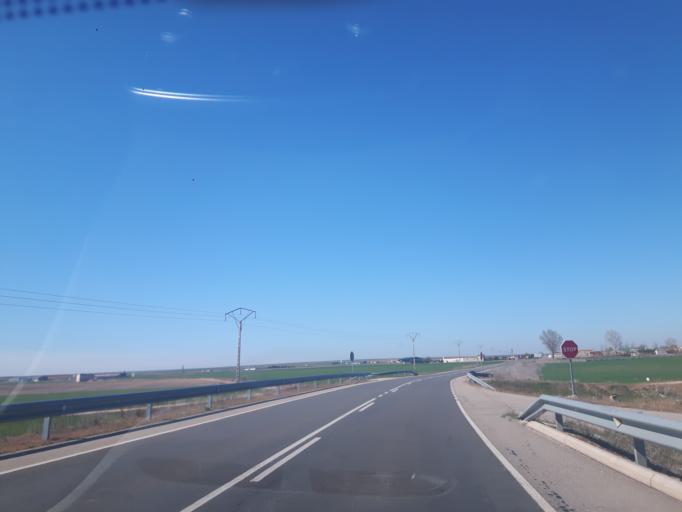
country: ES
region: Castille and Leon
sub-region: Provincia de Salamanca
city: Nava de Sotrobal
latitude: 40.8877
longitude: -5.2748
